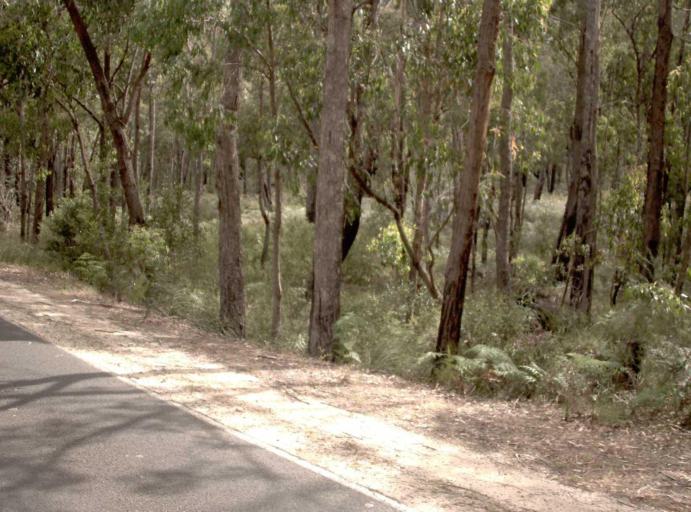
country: AU
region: Victoria
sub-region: Latrobe
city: Traralgon
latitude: -38.4189
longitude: 146.8166
